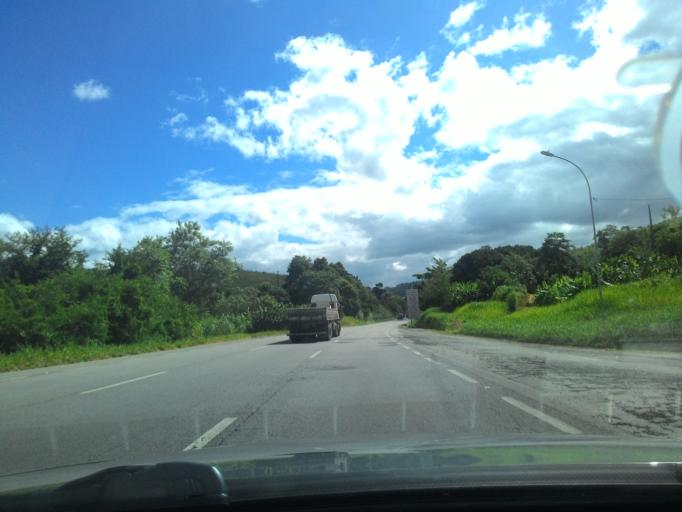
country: BR
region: Sao Paulo
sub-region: Cajati
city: Cajati
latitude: -24.7806
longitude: -48.1747
